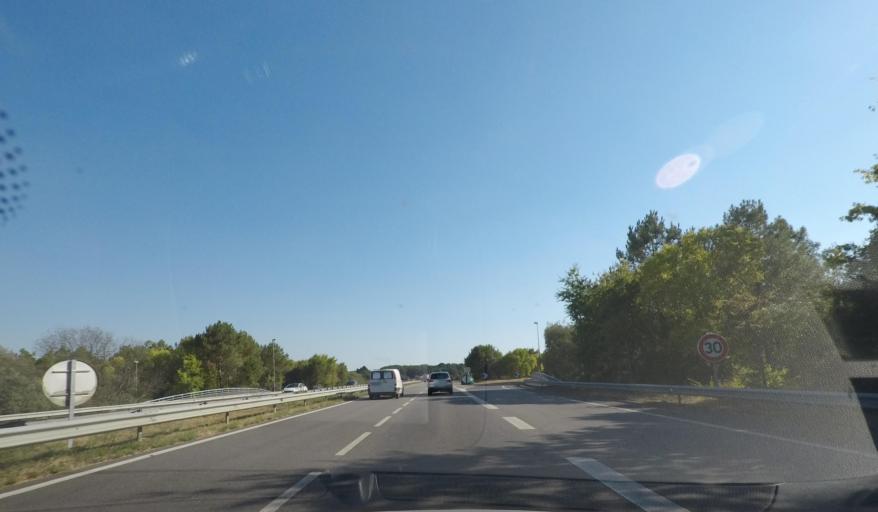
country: FR
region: Pays de la Loire
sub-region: Departement de la Loire-Atlantique
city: Saint-Michel-Chef-Chef
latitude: 47.2149
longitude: -2.1510
